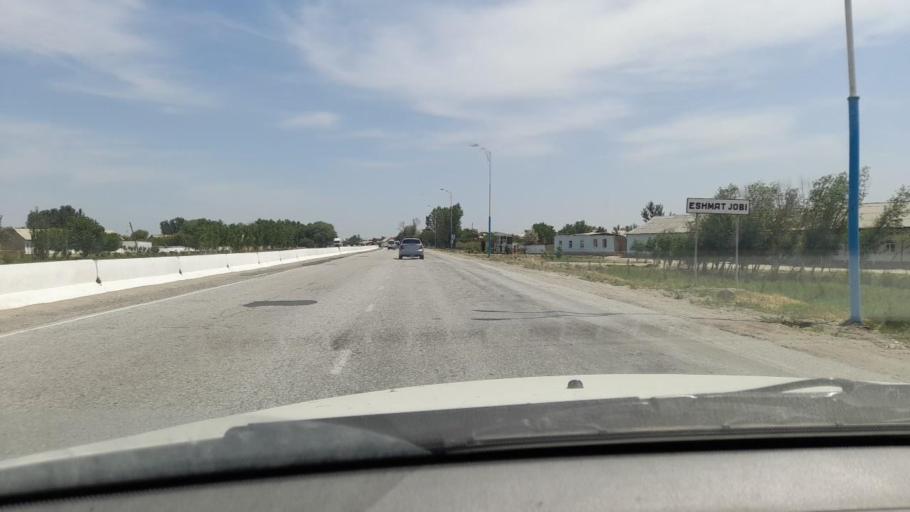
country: UZ
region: Navoiy
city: Navoiy
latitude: 40.1159
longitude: 65.4956
